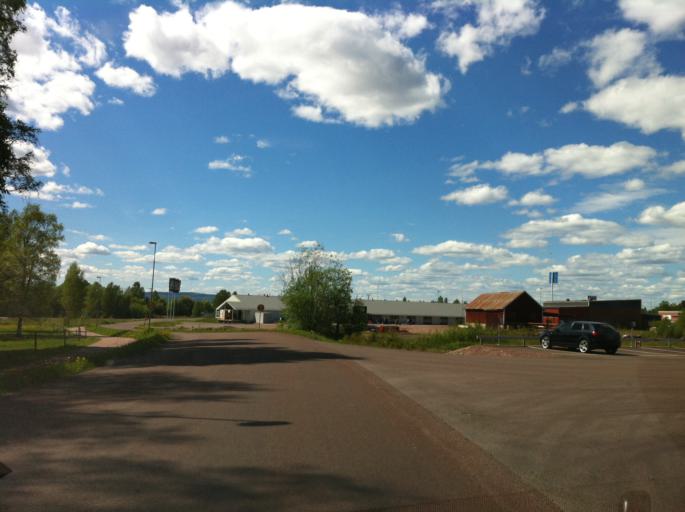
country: SE
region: Dalarna
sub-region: Mora Kommun
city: Mora
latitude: 61.0050
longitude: 14.6027
